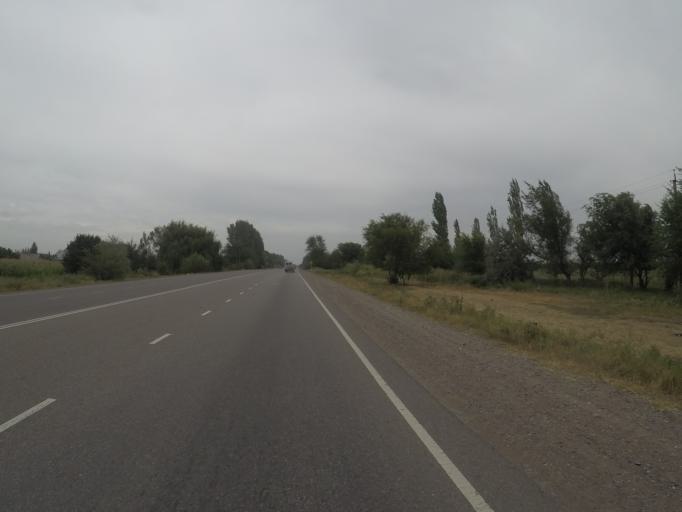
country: KG
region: Chuy
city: Bystrovka
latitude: 42.8192
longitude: 75.5748
